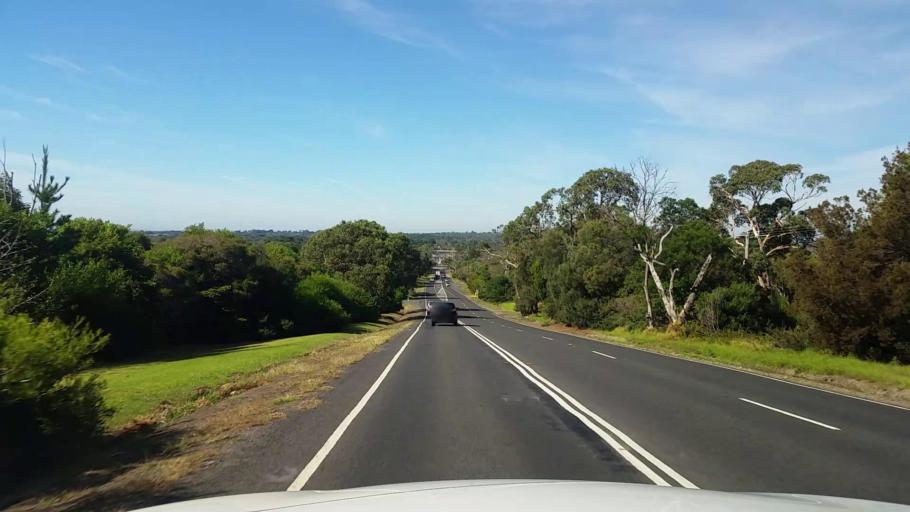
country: AU
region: Victoria
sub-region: Mornington Peninsula
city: Baxter
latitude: -38.1891
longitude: 145.1451
